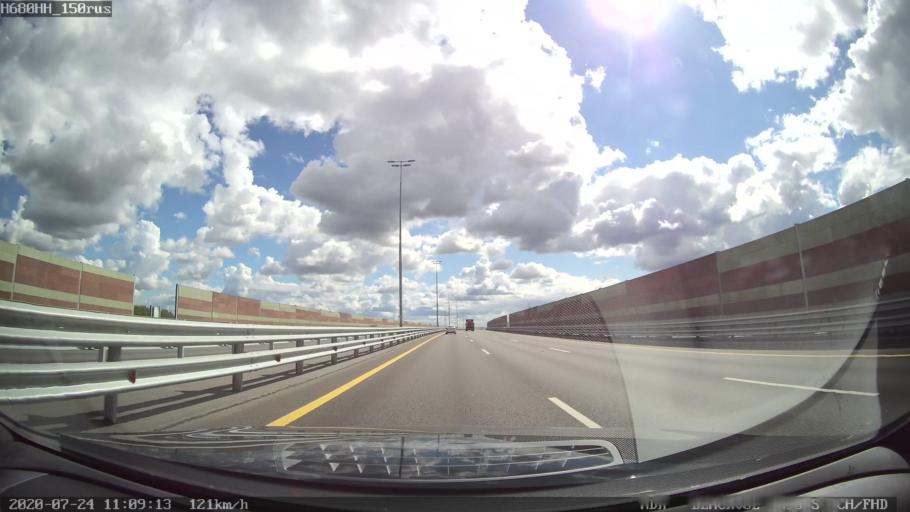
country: RU
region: St.-Petersburg
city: Tyarlevo
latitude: 59.7503
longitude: 30.4675
